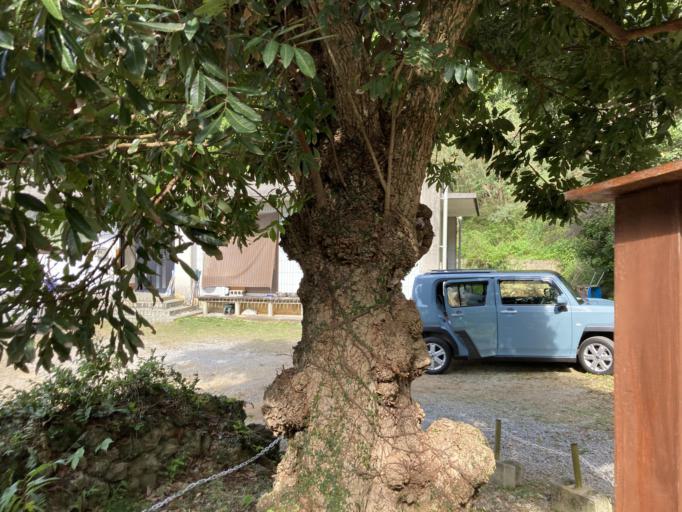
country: JP
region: Okinawa
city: Nago
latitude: 26.6997
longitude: 127.9305
